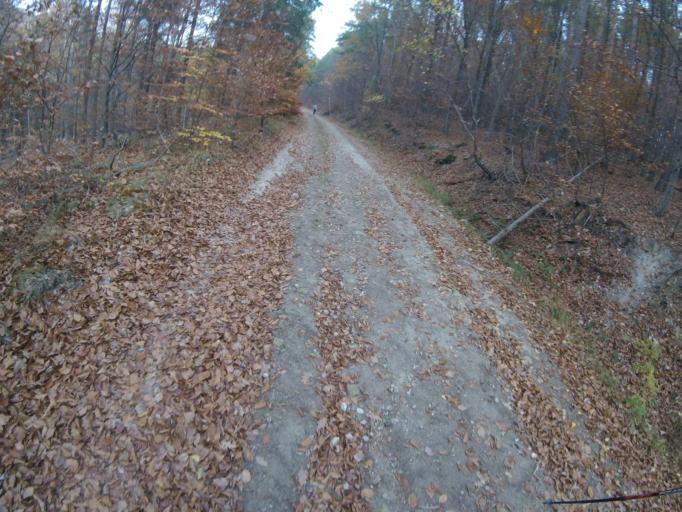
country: HU
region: Borsod-Abauj-Zemplen
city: Tolcsva
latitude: 48.4019
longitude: 21.4627
